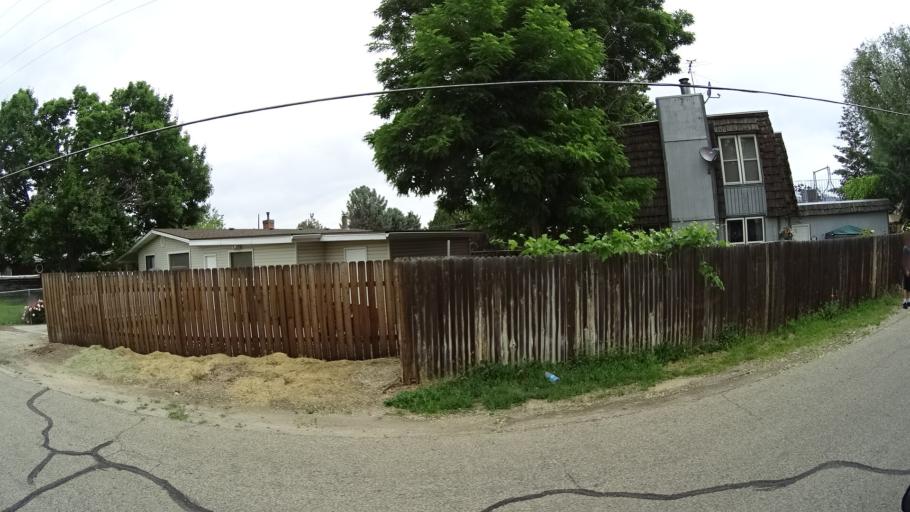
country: US
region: Idaho
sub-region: Ada County
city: Boise
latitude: 43.5717
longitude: -116.2107
